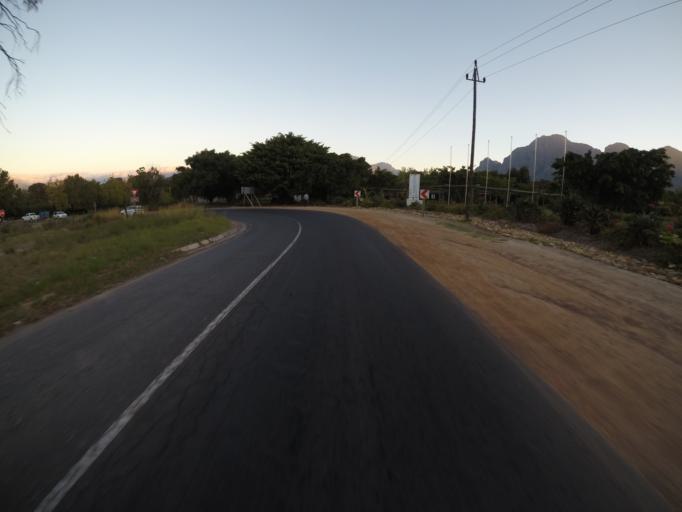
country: ZA
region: Western Cape
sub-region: Cape Winelands District Municipality
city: Paarl
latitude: -33.8364
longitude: 18.9531
